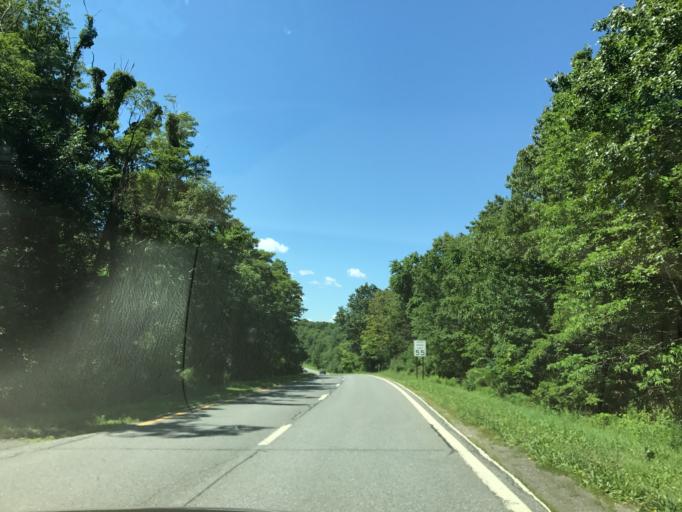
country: US
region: New York
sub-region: Dutchess County
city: Pine Plains
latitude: 41.9749
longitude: -73.7503
